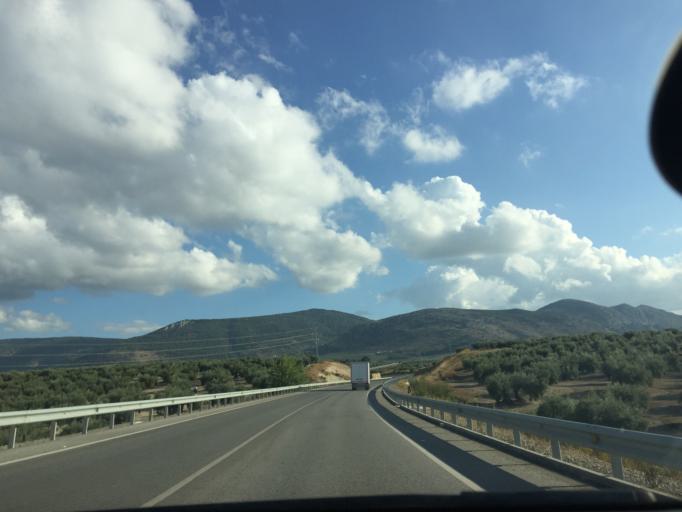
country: ES
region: Andalusia
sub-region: Provincia de Jaen
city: Mancha Real
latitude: 37.8023
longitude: -3.6252
